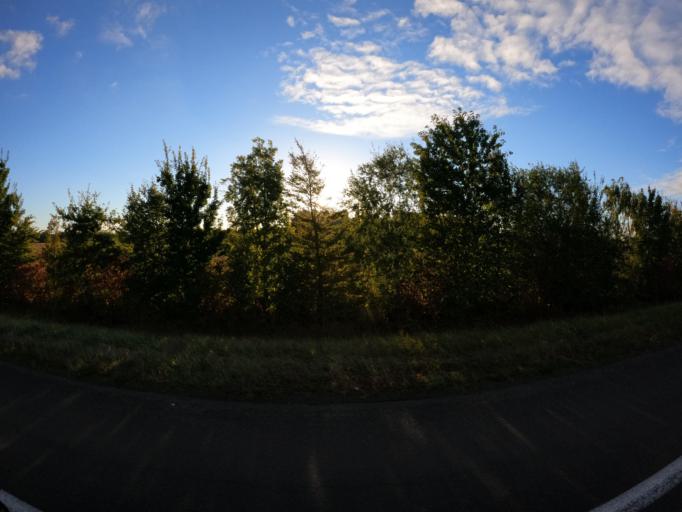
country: FR
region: Pays de la Loire
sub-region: Departement de Maine-et-Loire
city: Doue-la-Fontaine
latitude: 47.2282
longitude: -0.3088
